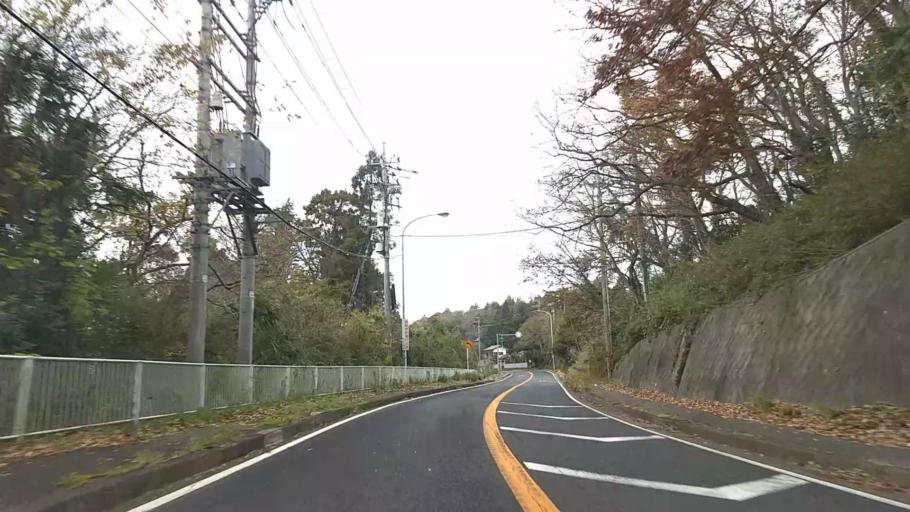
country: JP
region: Chiba
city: Yotsukaido
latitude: 35.5960
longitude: 140.2142
